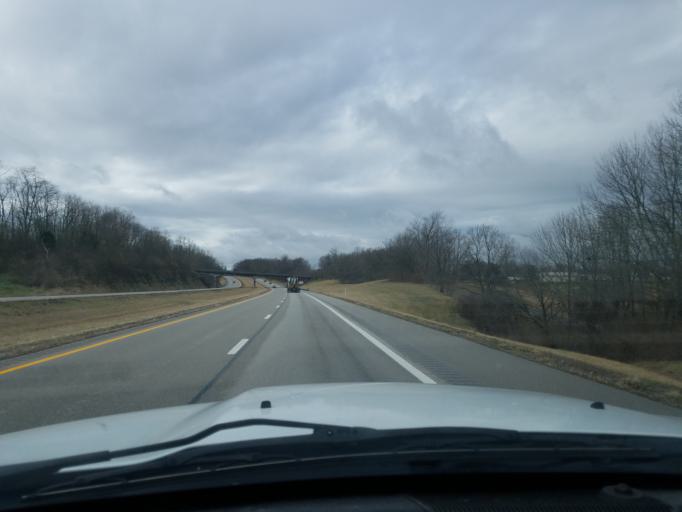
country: US
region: Kentucky
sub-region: Montgomery County
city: Mount Sterling
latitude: 38.0740
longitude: -83.9889
